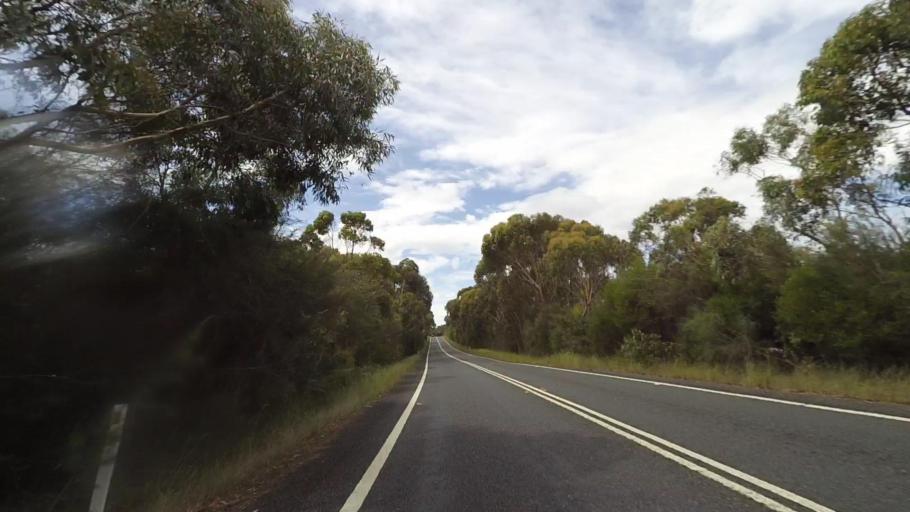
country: AU
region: New South Wales
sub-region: Sutherland Shire
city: Grays Point
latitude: -34.0925
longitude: 151.0633
